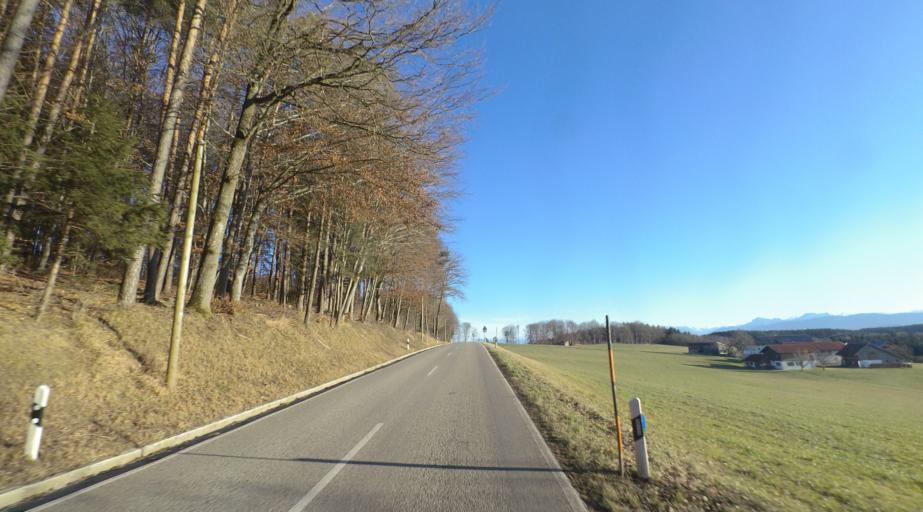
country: DE
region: Bavaria
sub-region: Upper Bavaria
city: Taching am See
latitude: 47.9976
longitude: 12.7037
